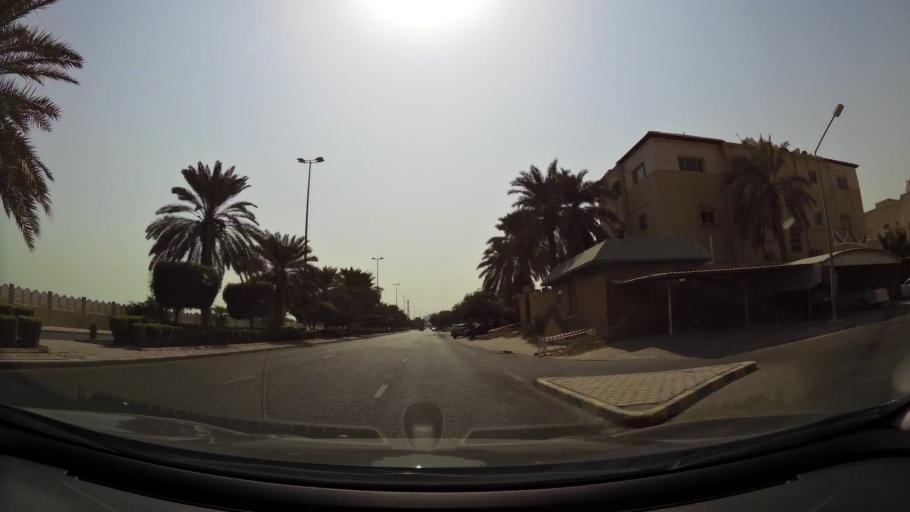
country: KW
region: Al Ahmadi
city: Al Fintas
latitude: 29.1750
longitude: 48.1224
